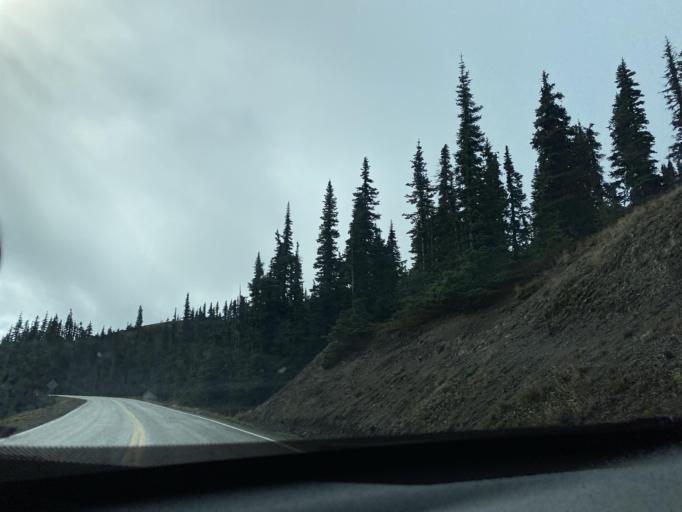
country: US
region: Washington
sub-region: Clallam County
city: Port Angeles
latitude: 47.9728
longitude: -123.4885
